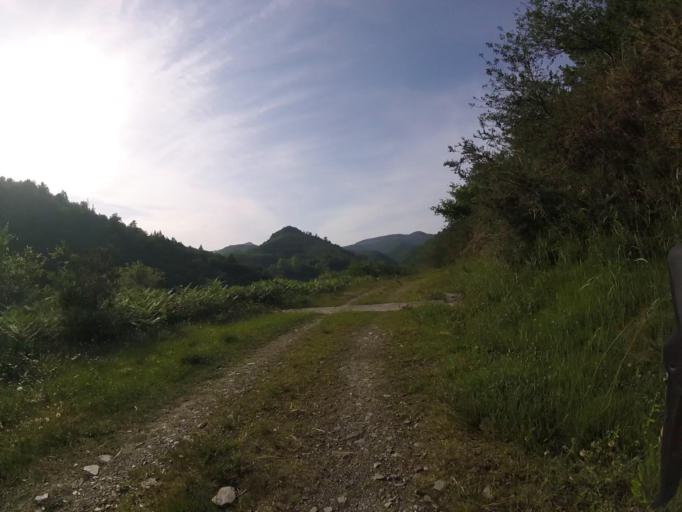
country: ES
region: Navarre
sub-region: Provincia de Navarra
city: Arano
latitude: 43.2269
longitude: -1.8658
